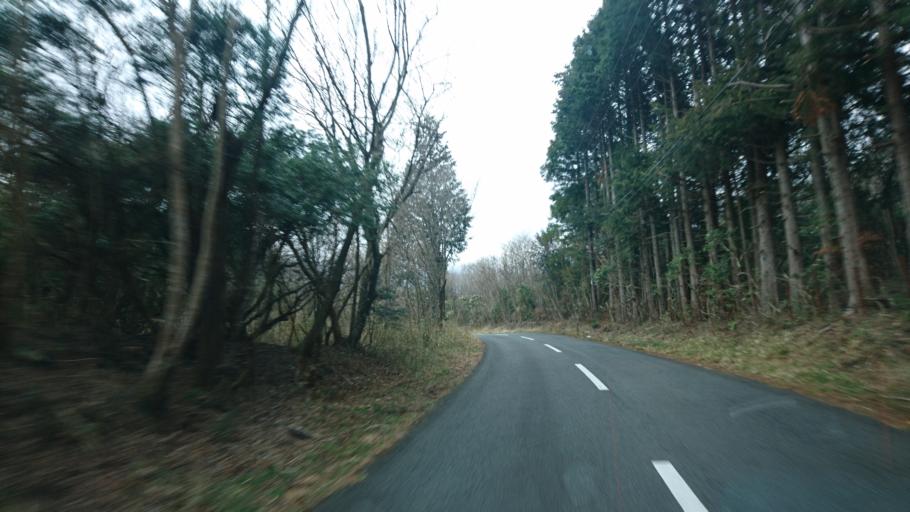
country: JP
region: Shizuoka
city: Fujinomiya
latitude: 35.3440
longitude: 138.5657
